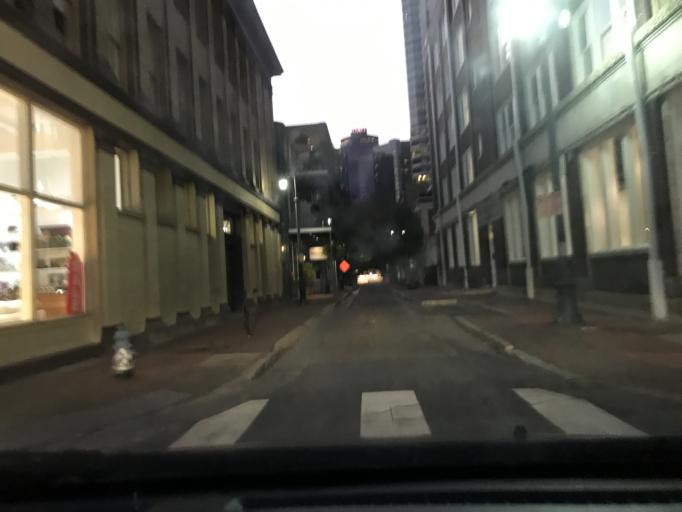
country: US
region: Louisiana
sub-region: Orleans Parish
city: New Orleans
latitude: 29.9489
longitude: -90.0735
